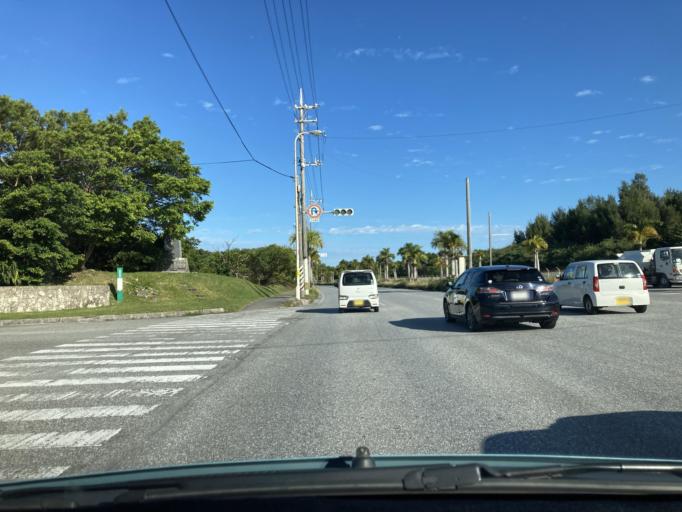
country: JP
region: Okinawa
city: Chatan
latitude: 26.3501
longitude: 127.7467
